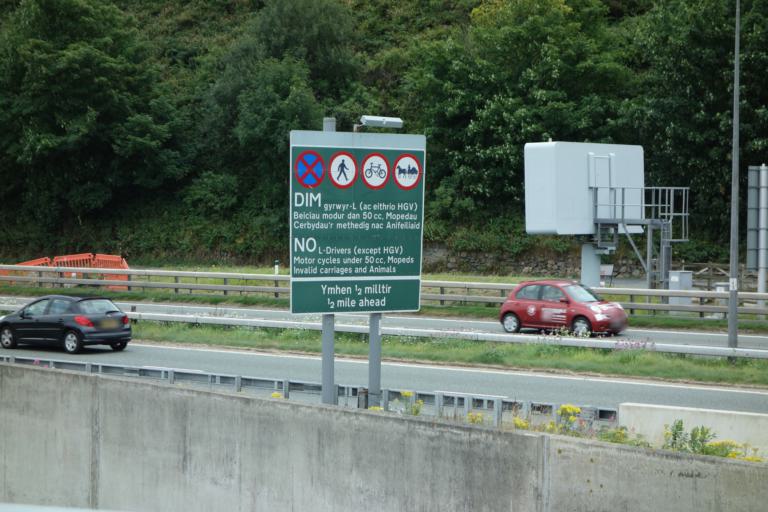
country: GB
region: Wales
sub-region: Conwy
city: Conwy
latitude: 53.2870
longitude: -3.8712
